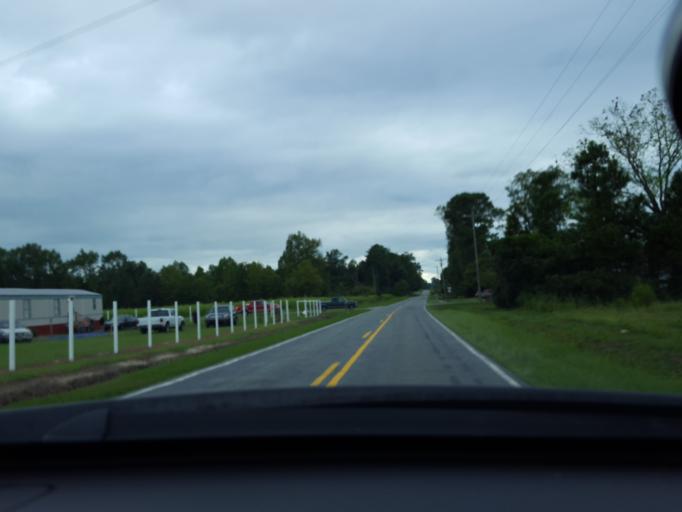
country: US
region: North Carolina
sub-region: Sampson County
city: Clinton
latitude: 34.7778
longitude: -78.3349
